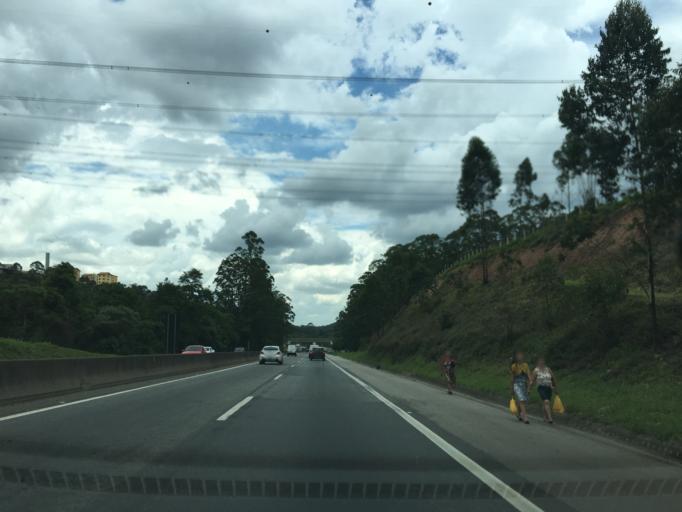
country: BR
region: Sao Paulo
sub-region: Mairipora
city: Mairipora
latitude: -23.2728
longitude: -46.5849
